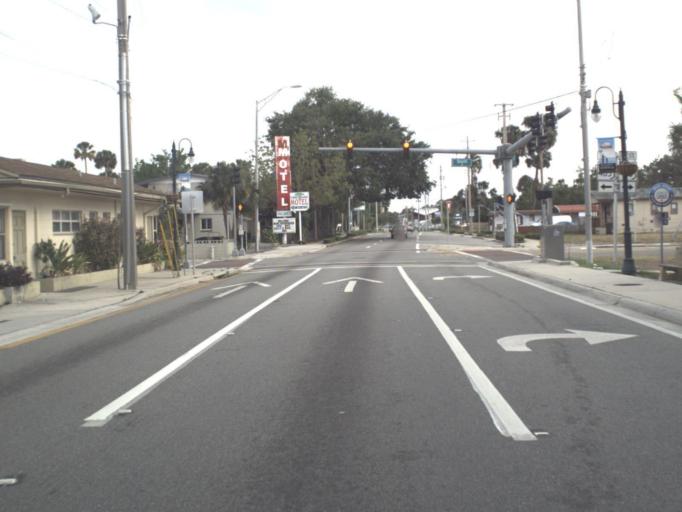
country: US
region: Florida
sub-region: Brevard County
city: Titusville
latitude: 28.6085
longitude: -80.8084
